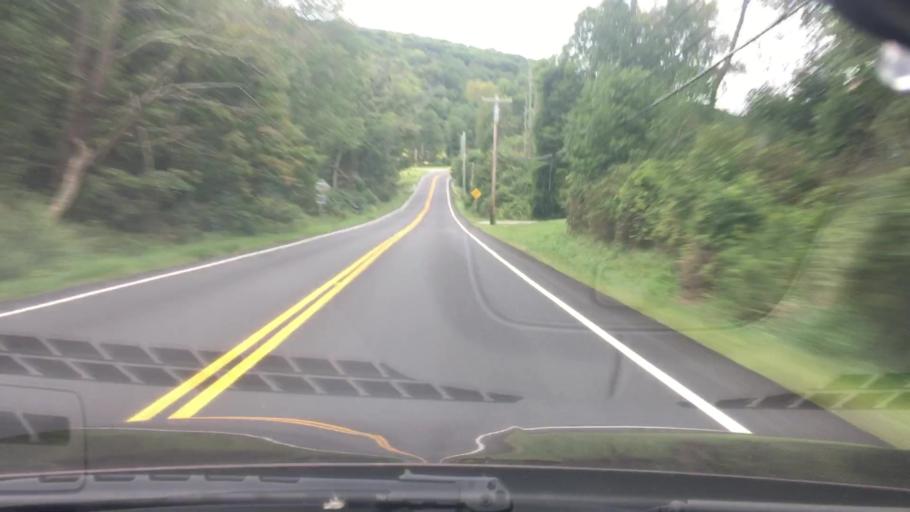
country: US
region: New York
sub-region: Dutchess County
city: Dover Plains
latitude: 41.8437
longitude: -73.5909
